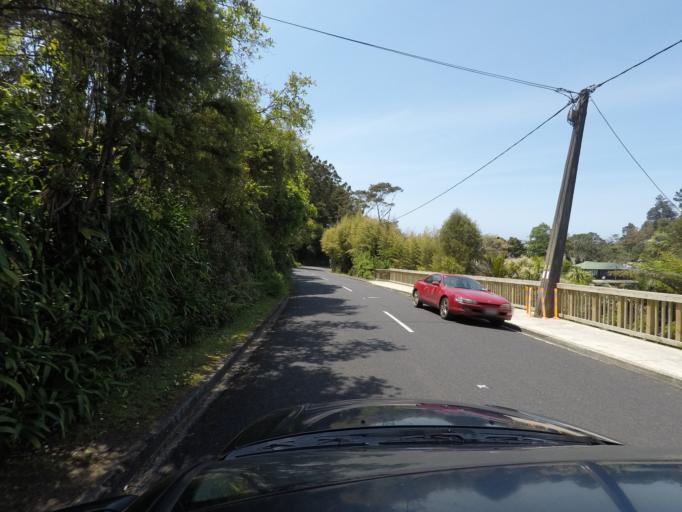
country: NZ
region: Auckland
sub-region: Auckland
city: Titirangi
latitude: -36.9662
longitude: 174.6402
